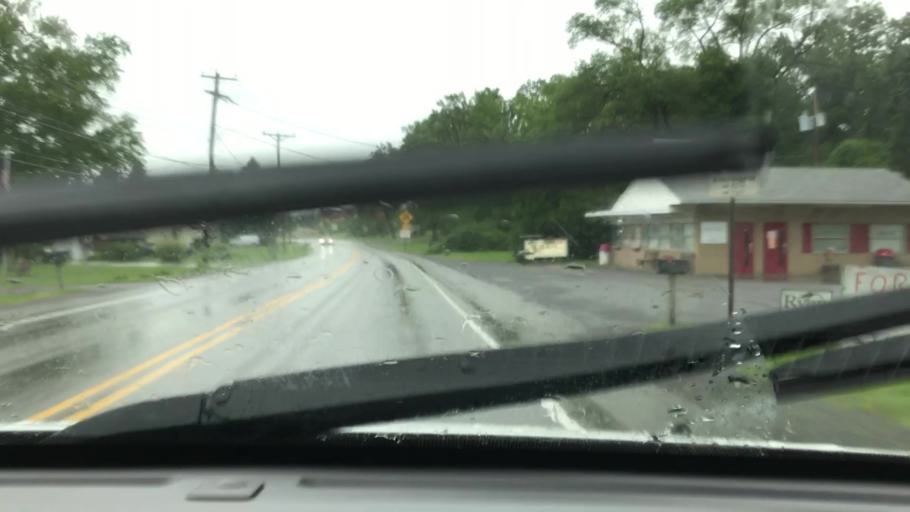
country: US
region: Pennsylvania
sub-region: Centre County
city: Philipsburg
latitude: 40.8793
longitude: -78.2126
